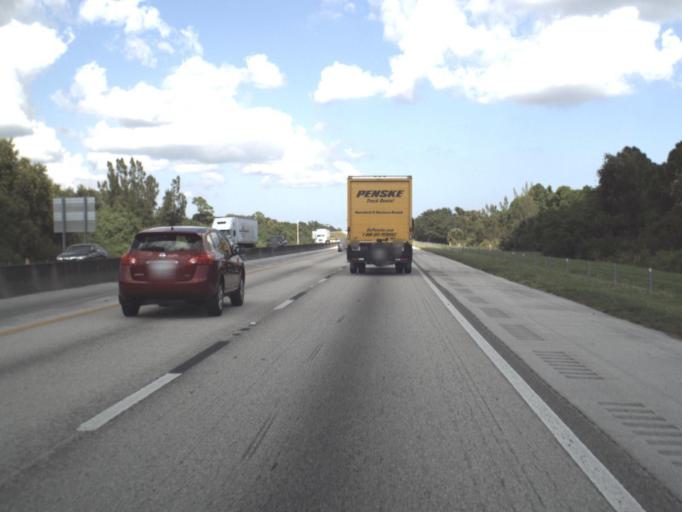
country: US
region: Florida
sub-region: Palm Beach County
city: Palm Beach Gardens
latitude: 26.8585
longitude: -80.1292
